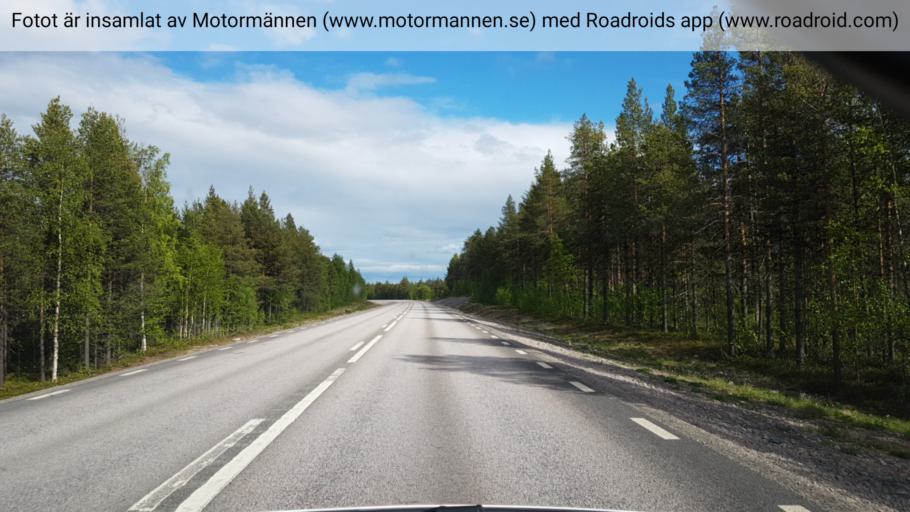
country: SE
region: Norrbotten
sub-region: Gallivare Kommun
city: Malmberget
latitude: 67.6583
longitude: 21.5266
